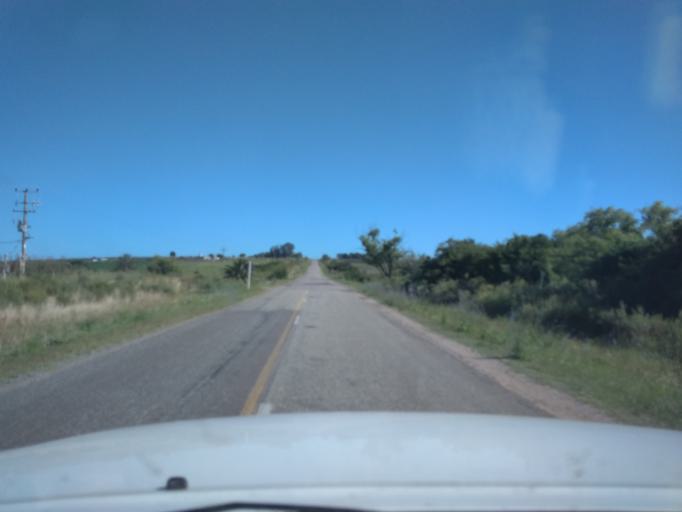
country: UY
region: Canelones
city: San Ramon
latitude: -34.1733
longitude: -55.9439
